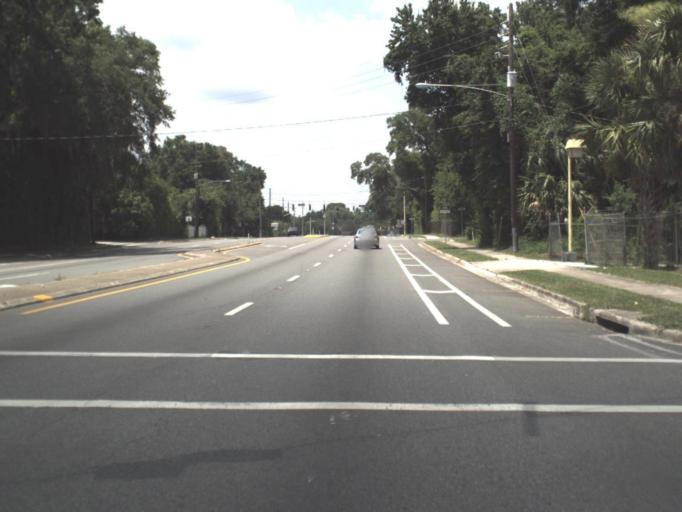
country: US
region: Florida
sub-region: Alachua County
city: Gainesville
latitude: 29.6482
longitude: -82.3114
